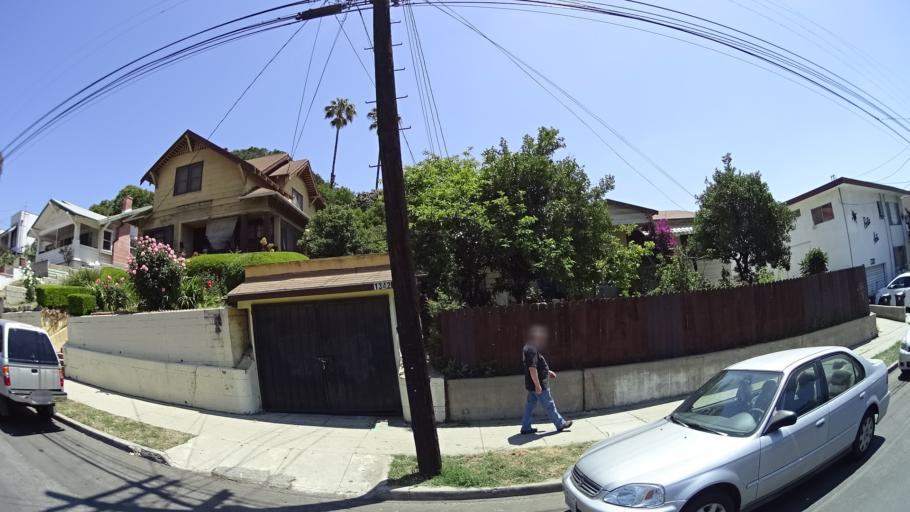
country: US
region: California
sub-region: Los Angeles County
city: Echo Park
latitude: 34.0766
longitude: -118.2537
